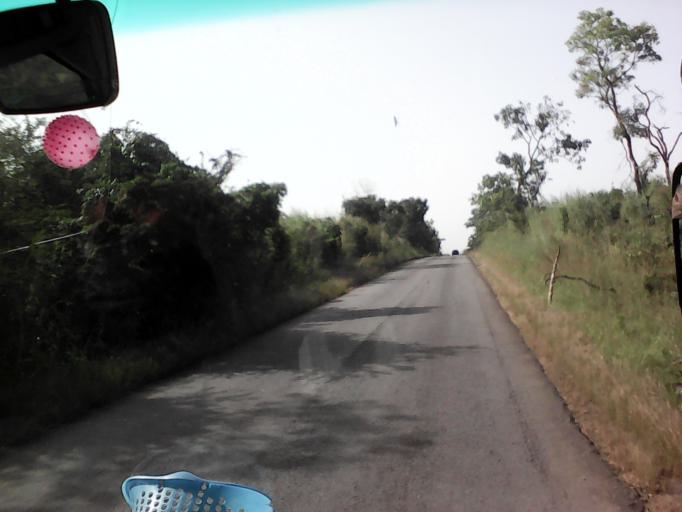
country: TG
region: Centrale
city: Sokode
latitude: 9.1184
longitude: 1.1458
